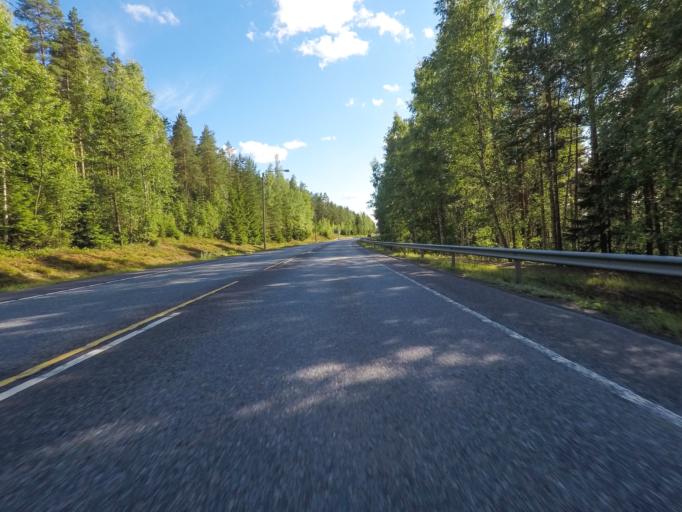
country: FI
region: Uusimaa
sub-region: Helsinki
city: Vihti
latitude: 60.3343
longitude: 24.2884
